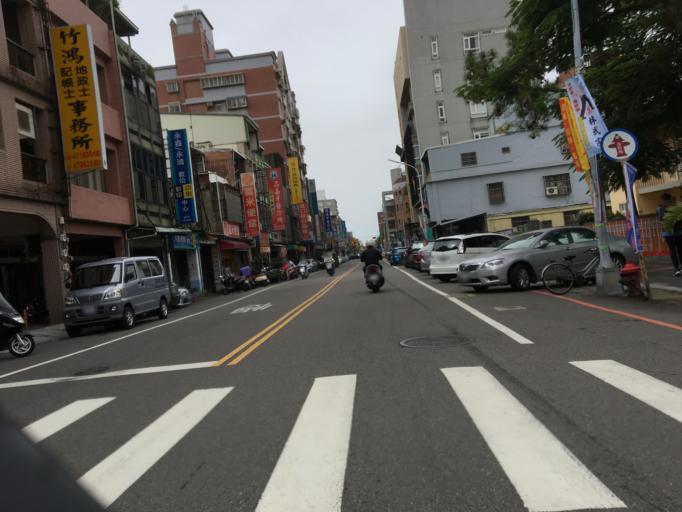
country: TW
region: Taiwan
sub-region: Miaoli
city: Miaoli
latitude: 24.6837
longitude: 120.8748
